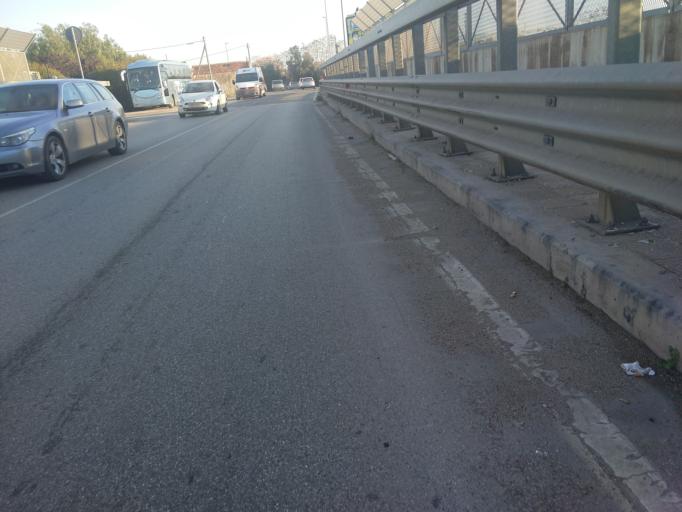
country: IT
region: Apulia
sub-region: Provincia di Bari
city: Bari
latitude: 41.1140
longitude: 16.8429
